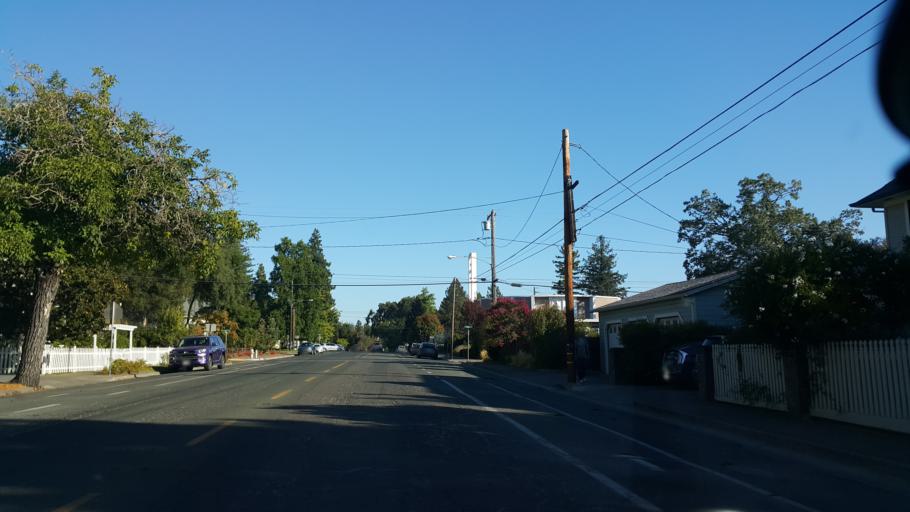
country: US
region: California
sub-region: Mendocino County
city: Ukiah
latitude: 39.1480
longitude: -123.2121
